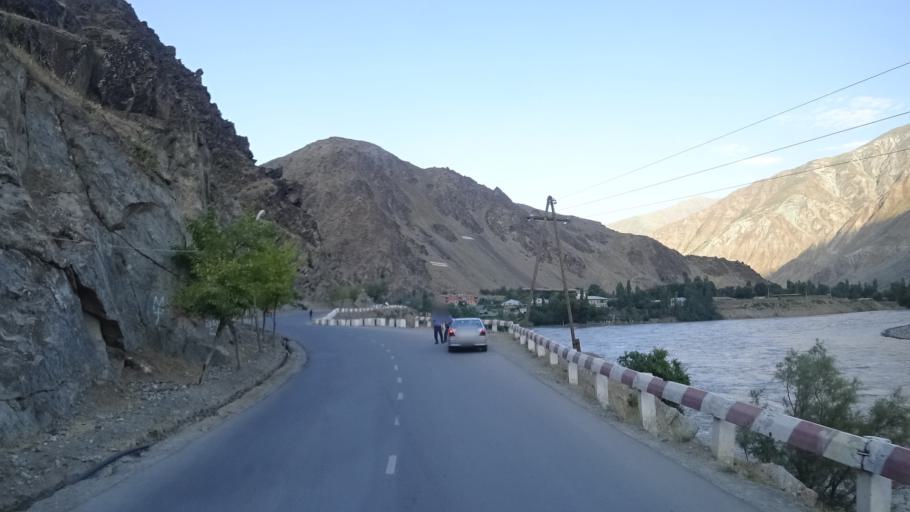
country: TJ
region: Gorno-Badakhshan
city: Qalaikhumb
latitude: 38.4565
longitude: 70.7834
